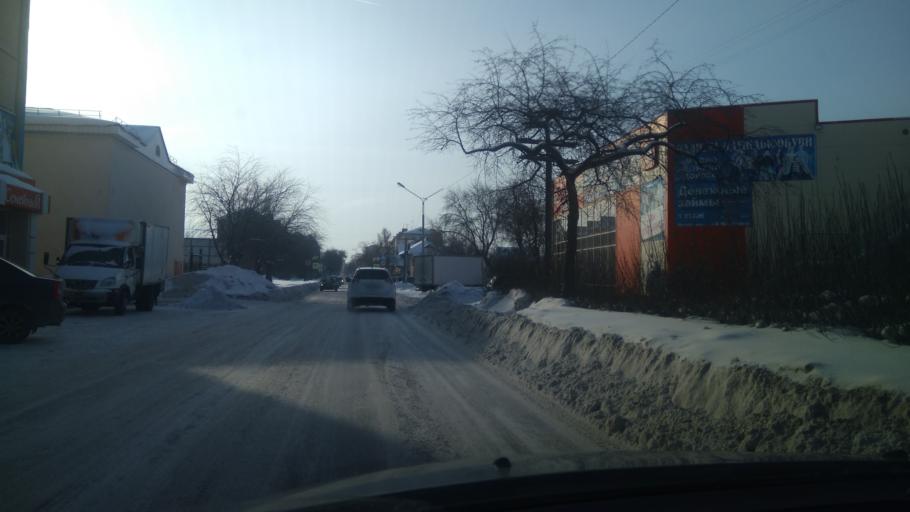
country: RU
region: Sverdlovsk
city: Sukhoy Log
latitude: 56.9058
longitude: 62.0331
